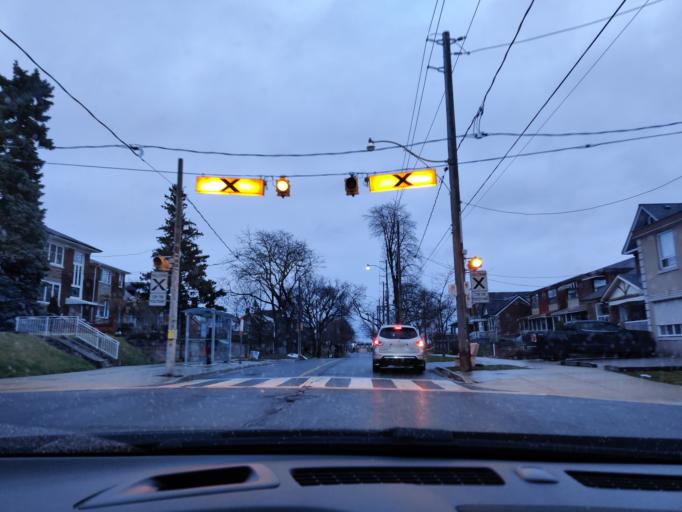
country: CA
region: Ontario
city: Toronto
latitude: 43.6779
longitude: -79.4558
